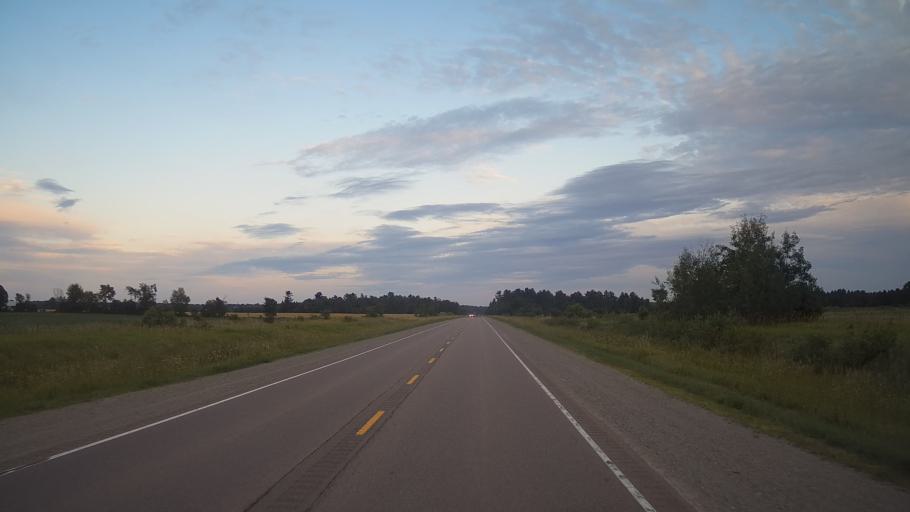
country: CA
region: Ontario
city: Pembroke
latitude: 45.7831
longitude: -77.1004
